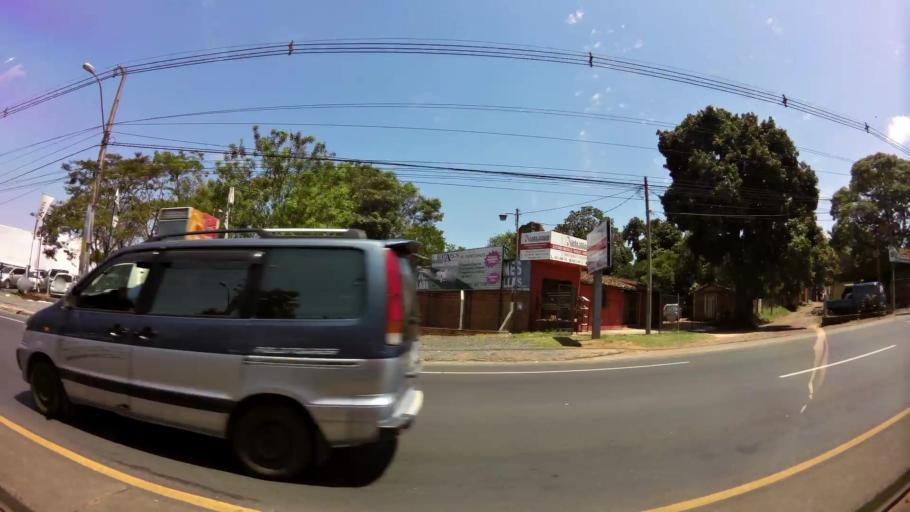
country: PY
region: Central
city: Nemby
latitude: -25.3819
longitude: -57.5523
